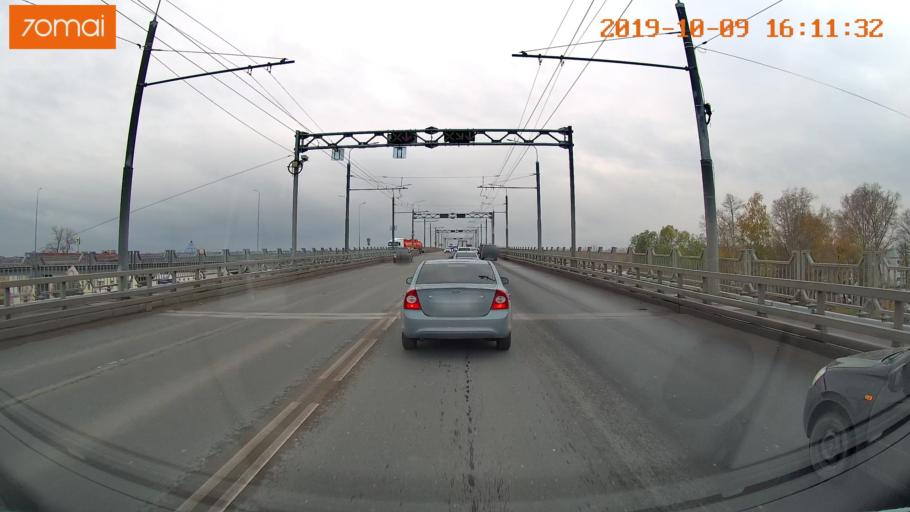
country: RU
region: Kostroma
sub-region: Kostromskoy Rayon
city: Kostroma
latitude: 57.7568
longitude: 40.9450
